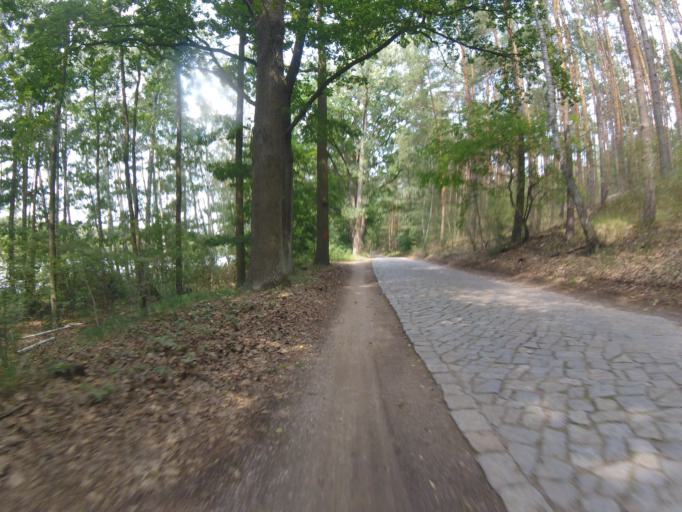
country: DE
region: Brandenburg
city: Schwerin
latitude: 52.1868
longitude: 13.5940
